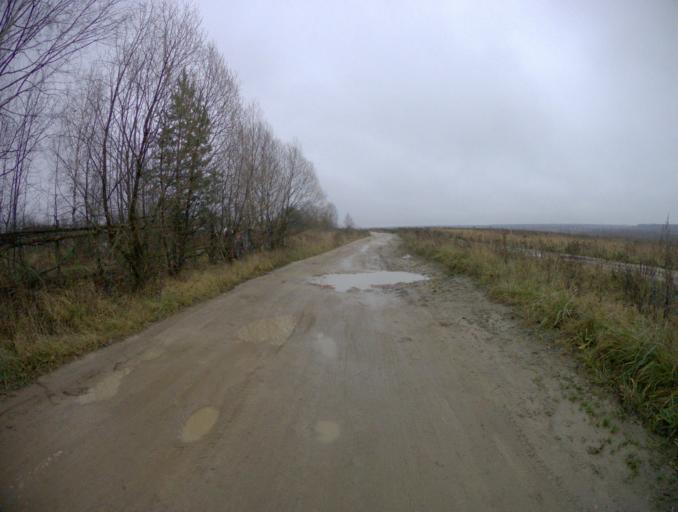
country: RU
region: Vladimir
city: Golovino
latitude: 55.9809
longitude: 40.4489
